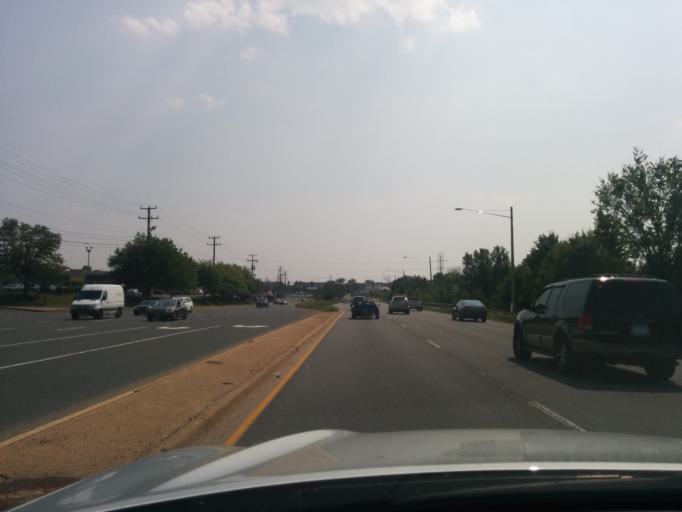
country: US
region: Virginia
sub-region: Fairfax County
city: Floris
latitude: 38.9519
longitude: -77.4099
